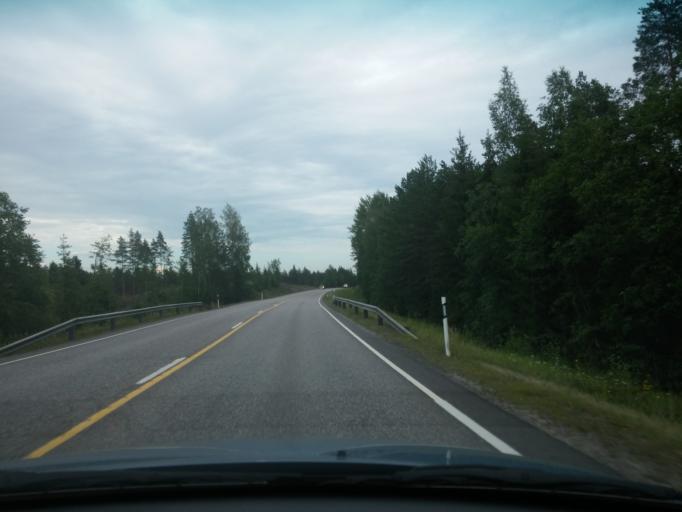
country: FI
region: Haeme
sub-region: Riihimaeki
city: Loppi
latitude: 60.7376
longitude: 24.3738
